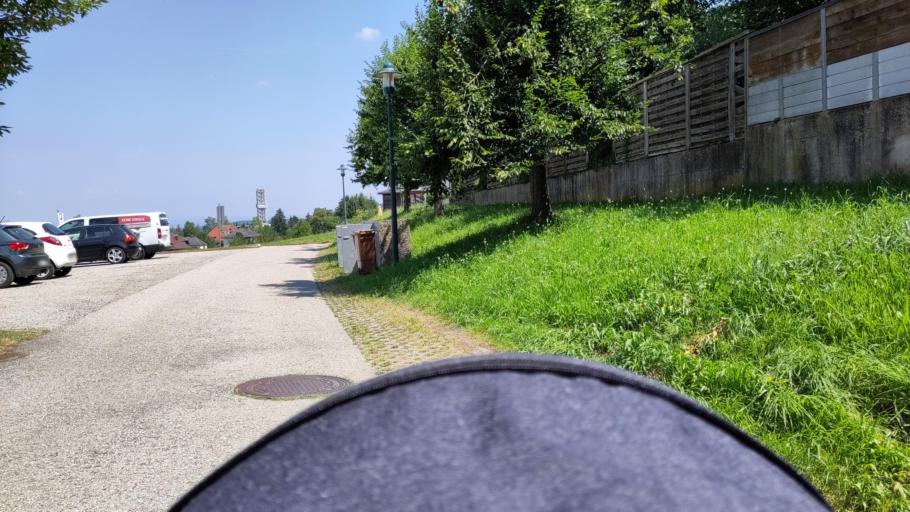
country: AT
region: Upper Austria
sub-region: Politischer Bezirk Steyr-Land
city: Sankt Ulrich bei Steyr
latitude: 48.0308
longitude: 14.4297
